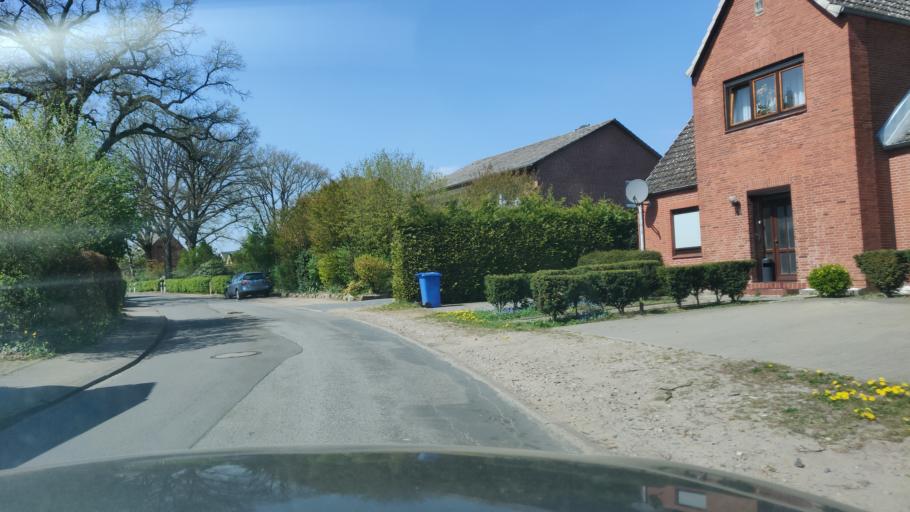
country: DE
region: Lower Saxony
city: Harmstorf
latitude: 53.3761
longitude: 9.9935
